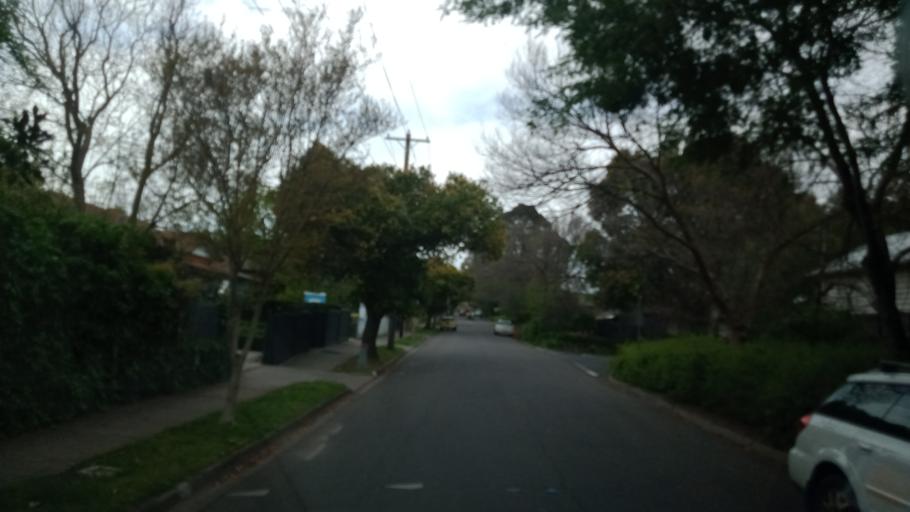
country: AU
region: Victoria
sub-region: Boroondara
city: Hawthorn East
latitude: -37.8277
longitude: 145.0398
